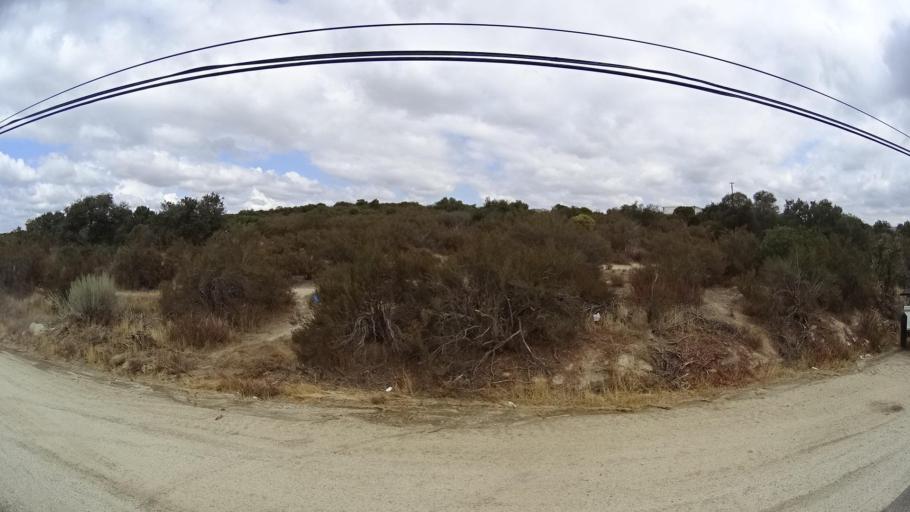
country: US
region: California
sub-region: San Diego County
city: Campo
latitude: 32.6349
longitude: -116.4771
